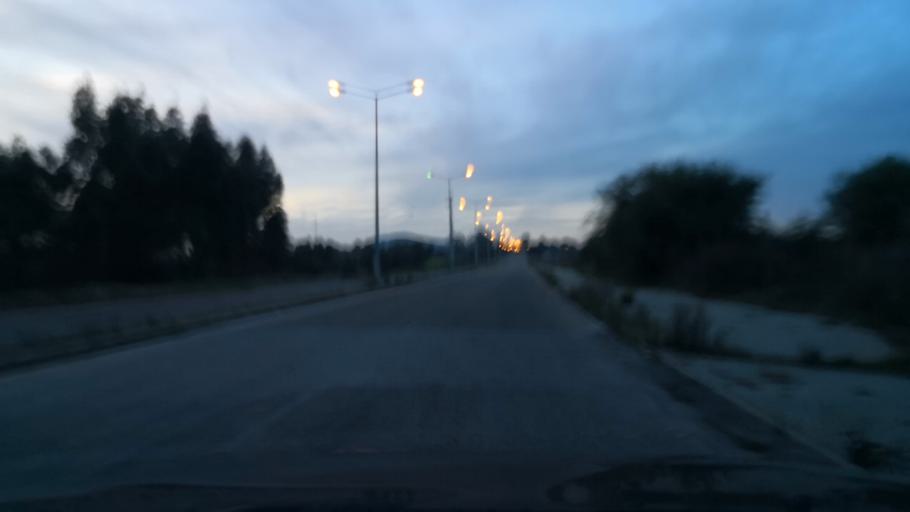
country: PT
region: Setubal
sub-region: Setubal
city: Setubal
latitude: 38.5140
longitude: -8.8532
